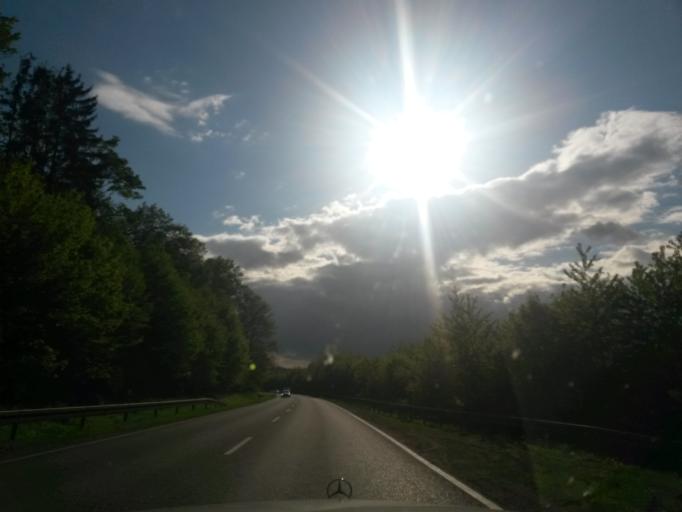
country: DE
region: Baden-Wuerttemberg
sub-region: Regierungsbezirk Stuttgart
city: Huttlingen
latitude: 48.8844
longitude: 10.1058
